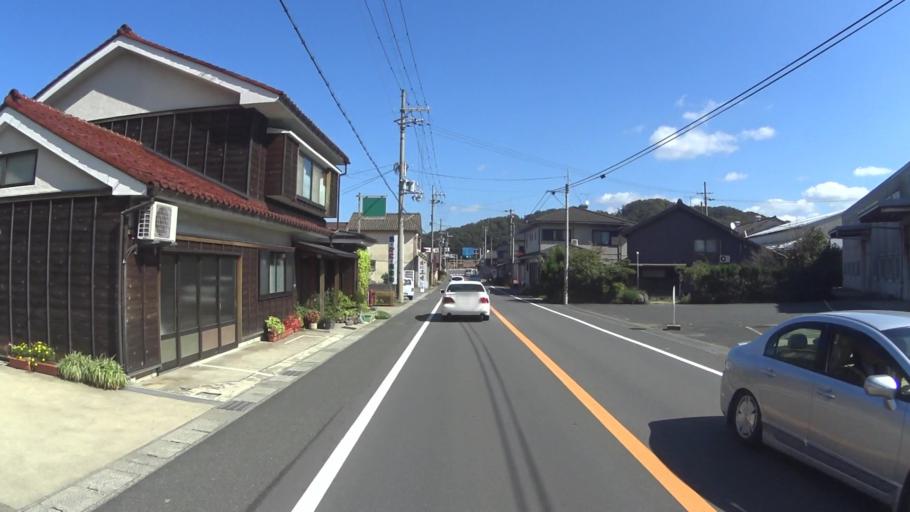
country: JP
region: Kyoto
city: Miyazu
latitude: 35.6679
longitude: 135.0253
